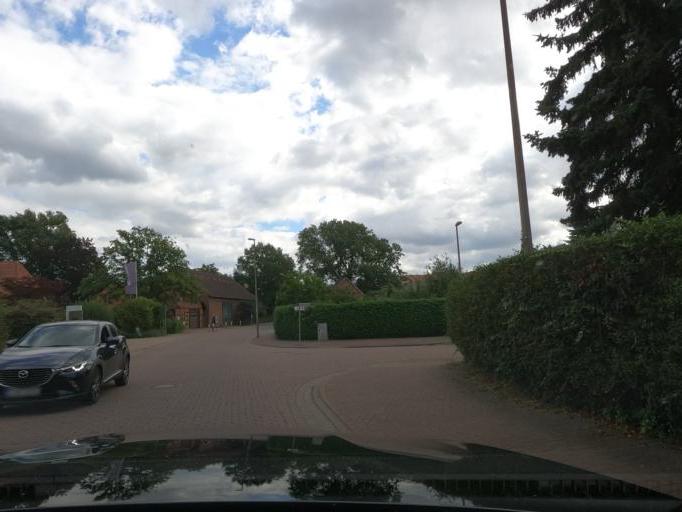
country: DE
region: Lower Saxony
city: Isernhagen Farster Bauerschaft
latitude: 52.4453
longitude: 9.8959
